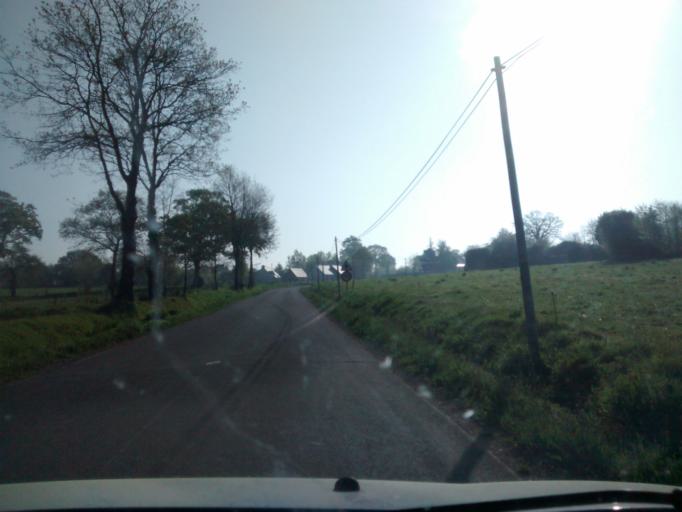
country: FR
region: Brittany
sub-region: Departement d'Ille-et-Vilaine
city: Saint-Jean-sur-Couesnon
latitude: 48.2783
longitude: -1.3610
